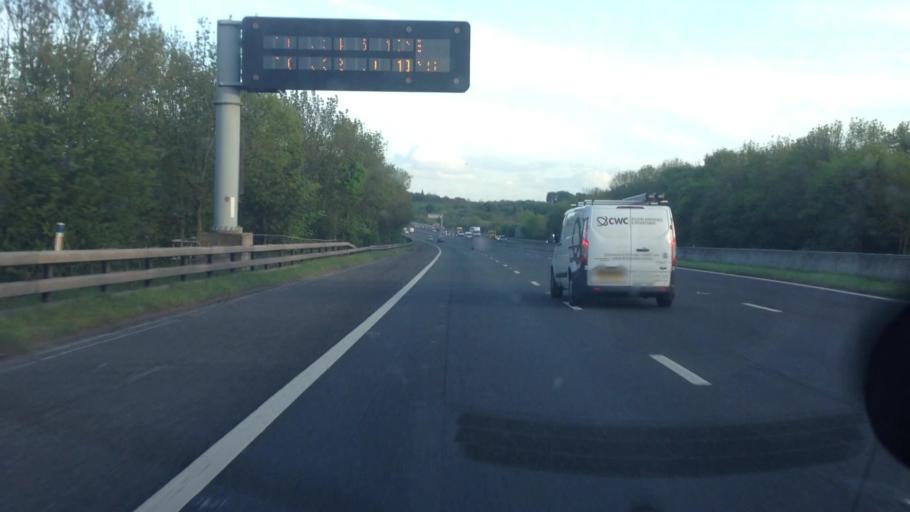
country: GB
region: England
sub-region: Barnsley
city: Hoyland Nether
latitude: 53.4885
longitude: -1.4687
